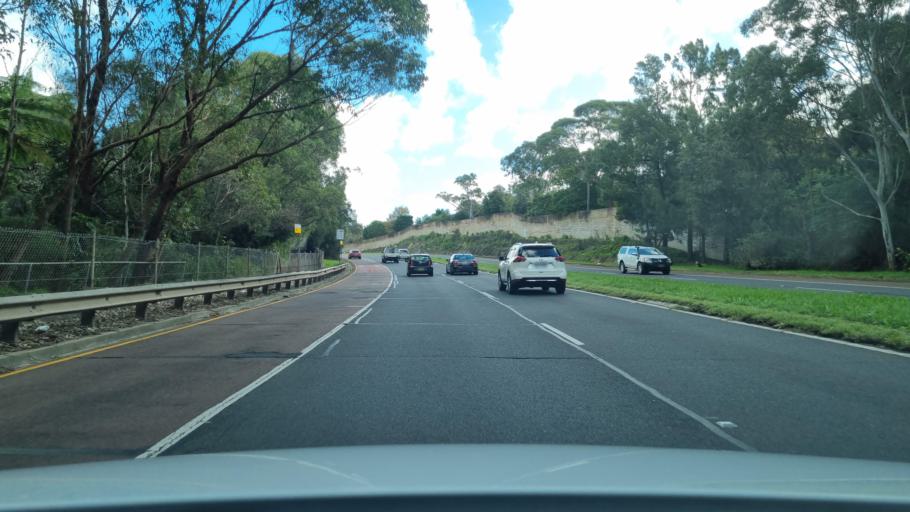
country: AU
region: New South Wales
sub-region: Manly Vale
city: Balgowlah
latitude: -33.7887
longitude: 151.2599
